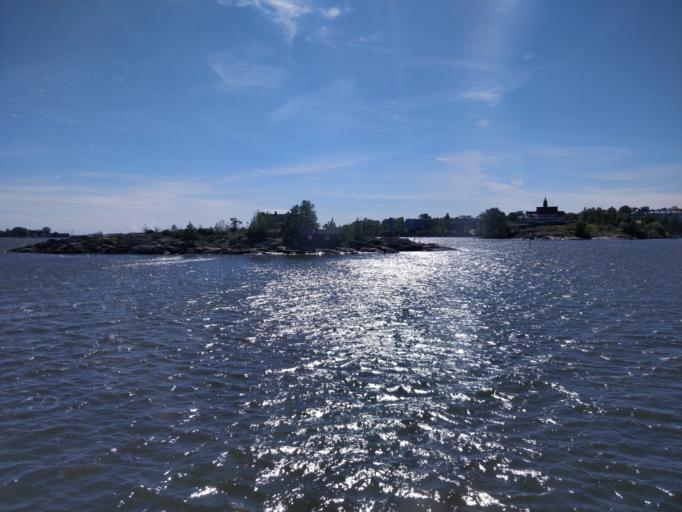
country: FI
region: Uusimaa
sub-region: Helsinki
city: Helsinki
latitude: 60.1610
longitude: 24.9742
